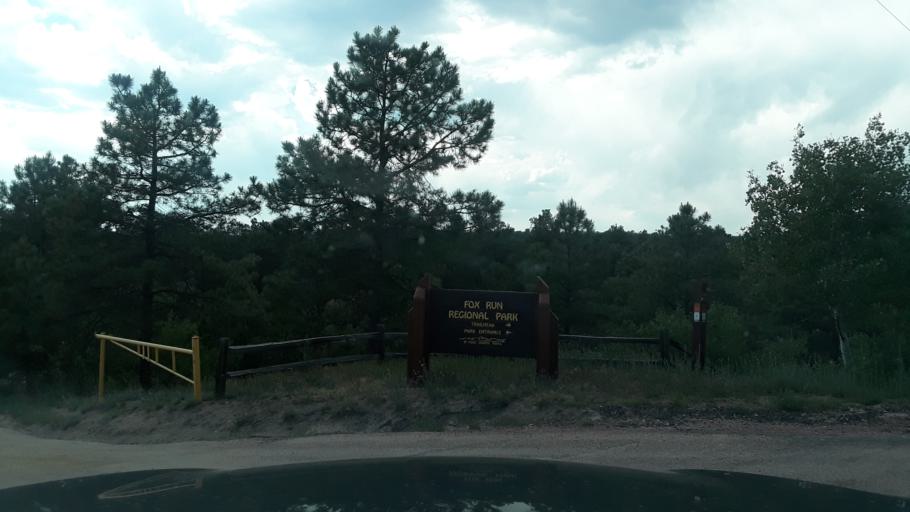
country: US
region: Colorado
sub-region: El Paso County
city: Gleneagle
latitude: 39.0590
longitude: -104.7850
